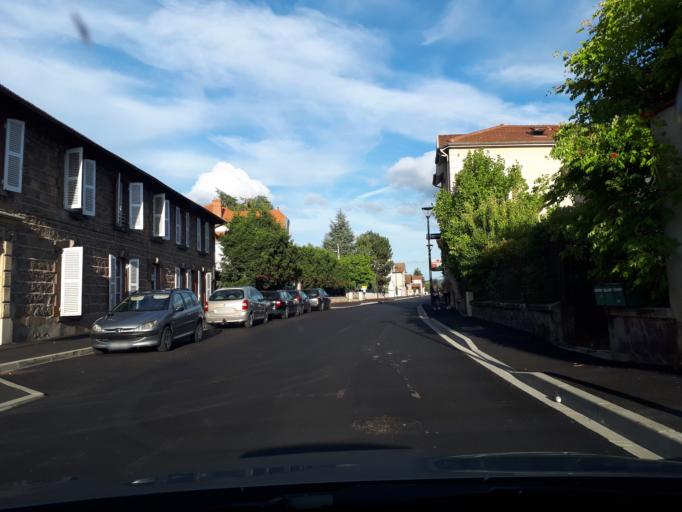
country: FR
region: Rhone-Alpes
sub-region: Departement de la Loire
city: Feurs
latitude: 45.7443
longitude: 4.2319
